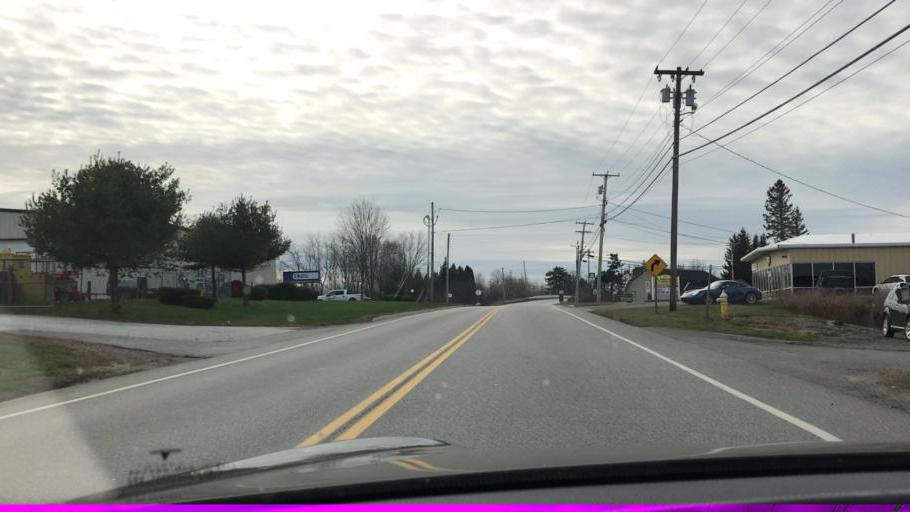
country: US
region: Maine
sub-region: Penobscot County
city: Bangor
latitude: 44.7827
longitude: -68.8160
